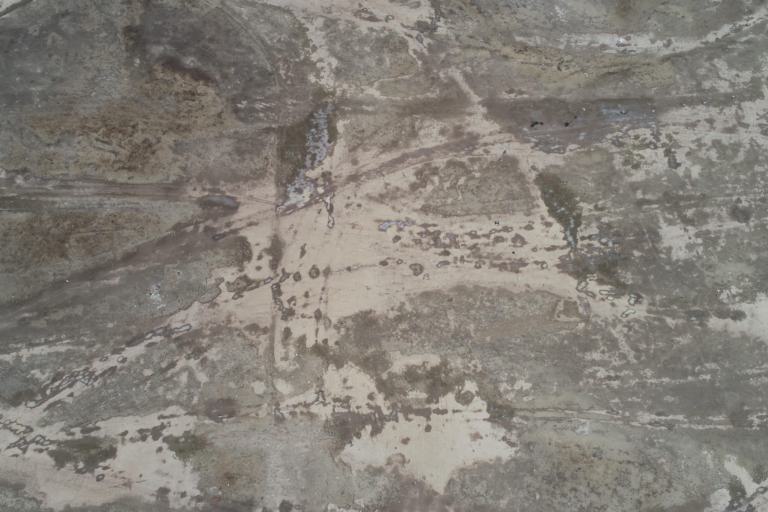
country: BO
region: La Paz
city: Achacachi
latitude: -16.0536
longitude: -68.6873
